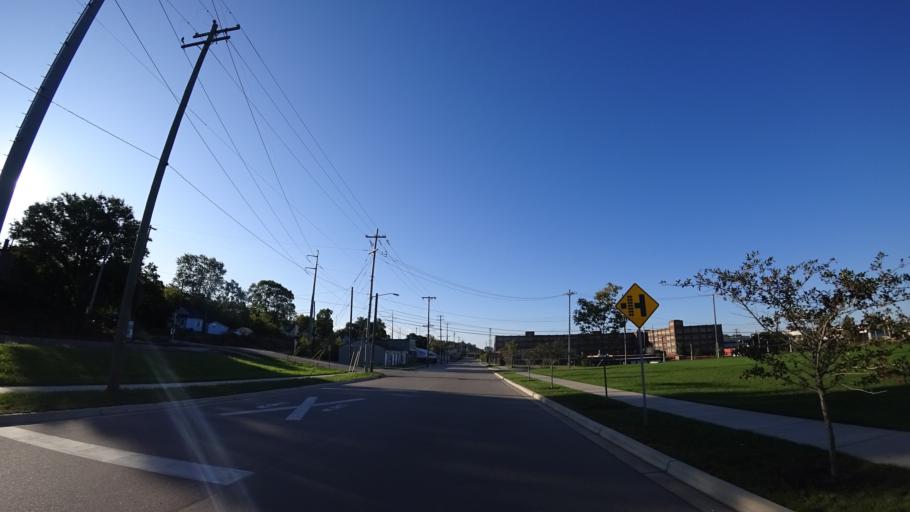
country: US
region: Michigan
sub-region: Kent County
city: Grand Rapids
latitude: 42.9892
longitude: -85.6688
